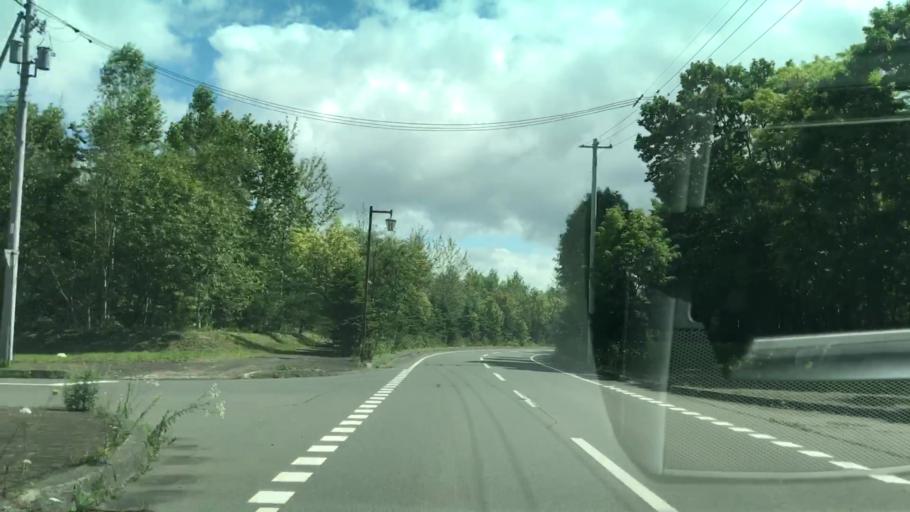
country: JP
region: Hokkaido
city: Chitose
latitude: 42.7790
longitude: 141.6020
